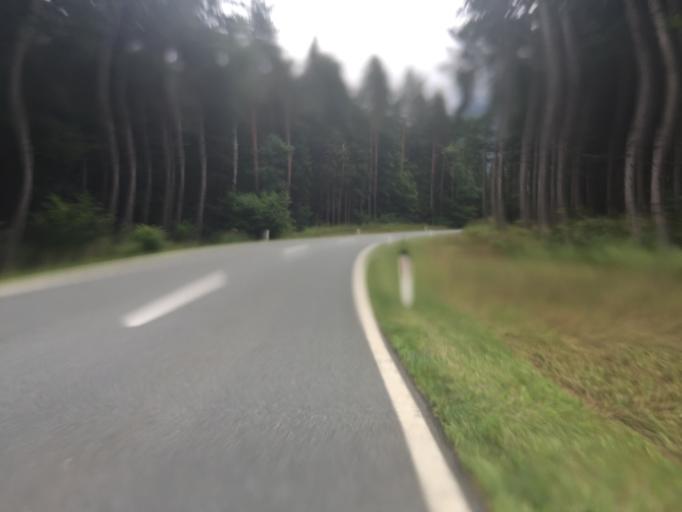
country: AT
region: Carinthia
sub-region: Politischer Bezirk Volkermarkt
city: Feistritz ob Bleiburg
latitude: 46.5467
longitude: 14.7724
